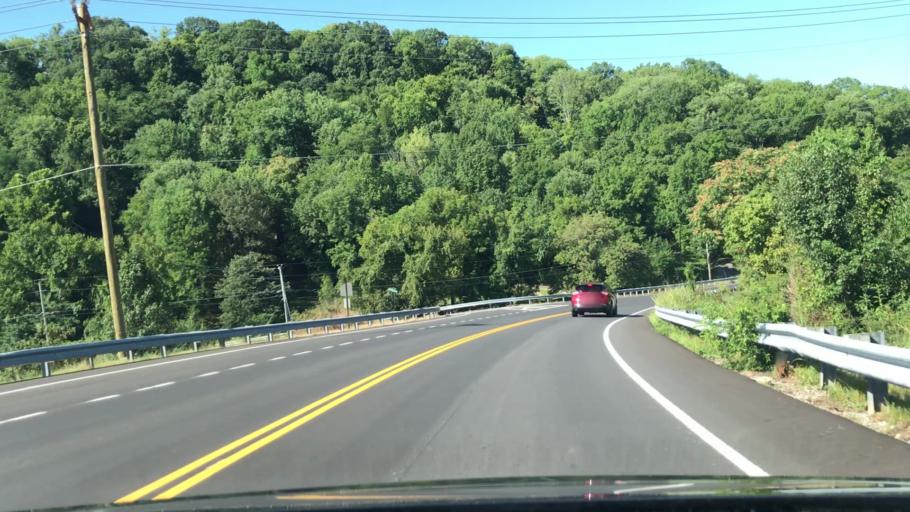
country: US
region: Tennessee
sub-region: Williamson County
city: Franklin
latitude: 35.9725
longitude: -86.8602
